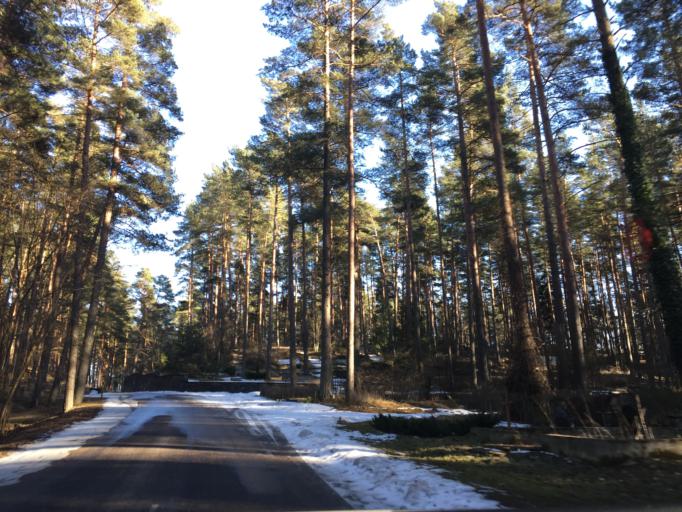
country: LV
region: Babite
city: Pinki
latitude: 56.9301
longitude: 23.9106
